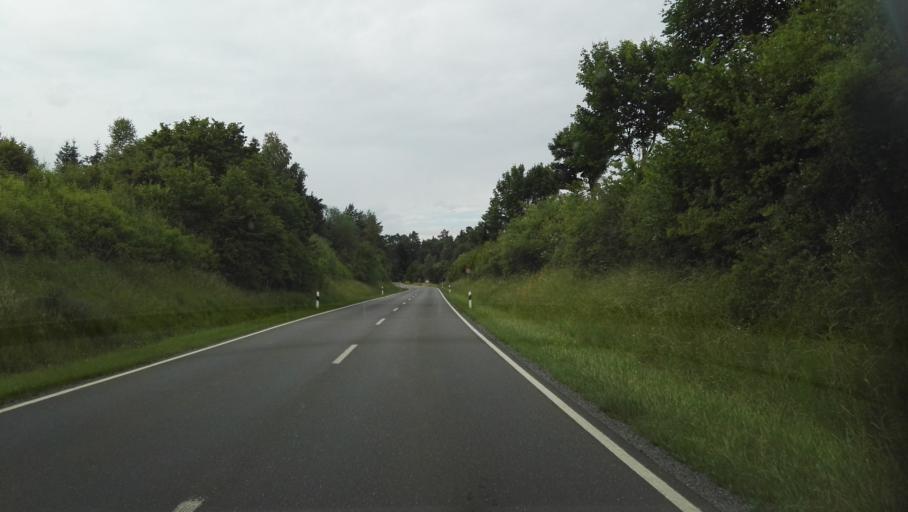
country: DE
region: Bavaria
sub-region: Upper Franconia
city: Hollfeld
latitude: 49.9234
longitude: 11.3052
